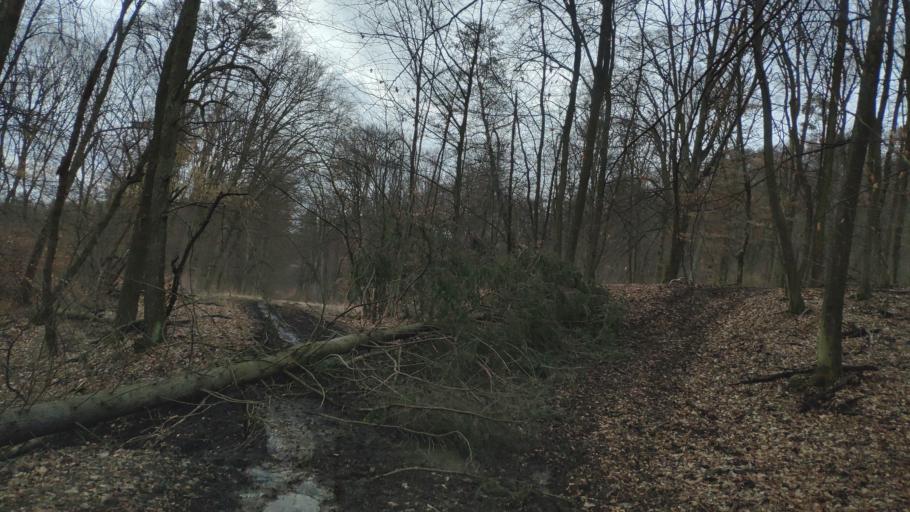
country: SK
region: Presovsky
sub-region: Okres Presov
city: Presov
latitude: 49.0706
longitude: 21.2829
